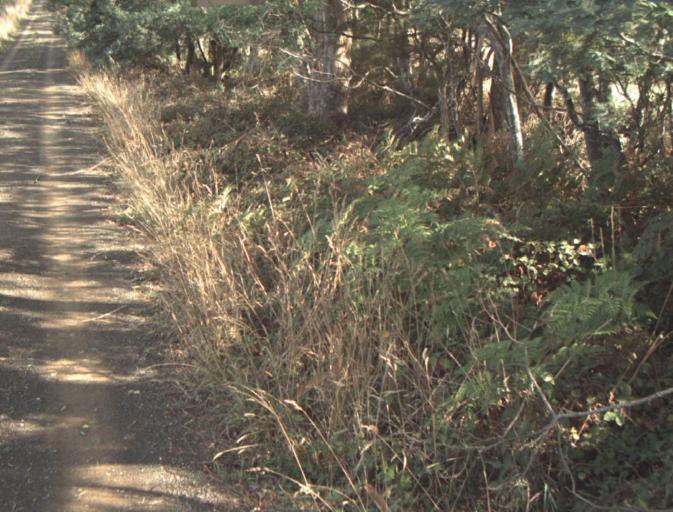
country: AU
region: Tasmania
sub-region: Launceston
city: Mayfield
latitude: -41.2091
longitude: 147.1500
